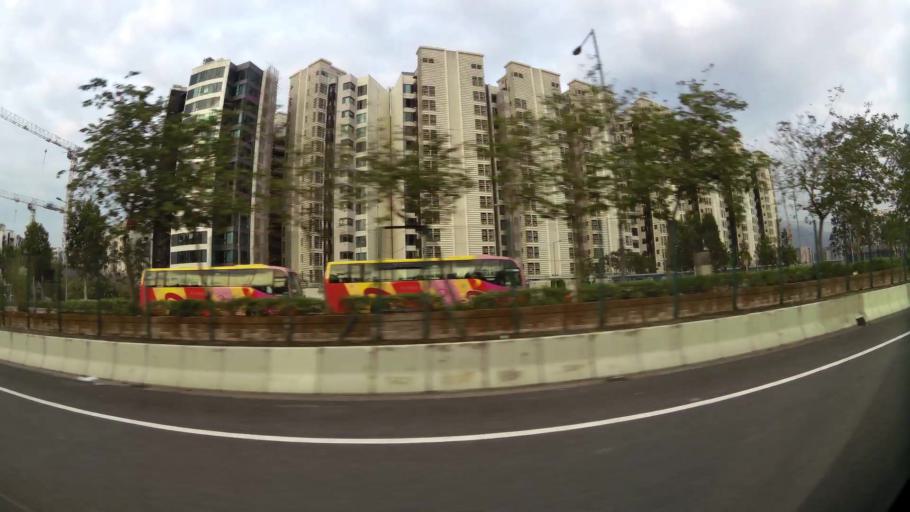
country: HK
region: Tai Po
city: Tai Po
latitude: 22.4317
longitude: 114.2012
